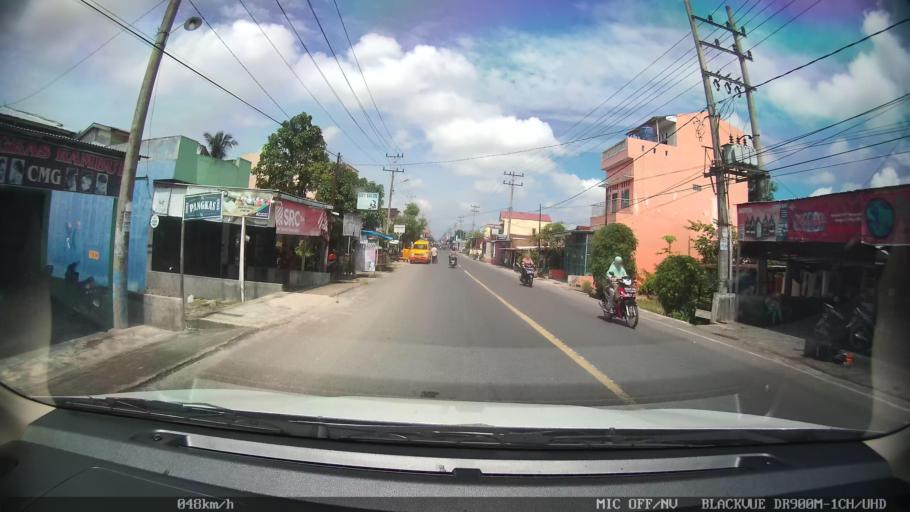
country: ID
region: North Sumatra
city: Percut
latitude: 3.6072
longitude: 98.7852
